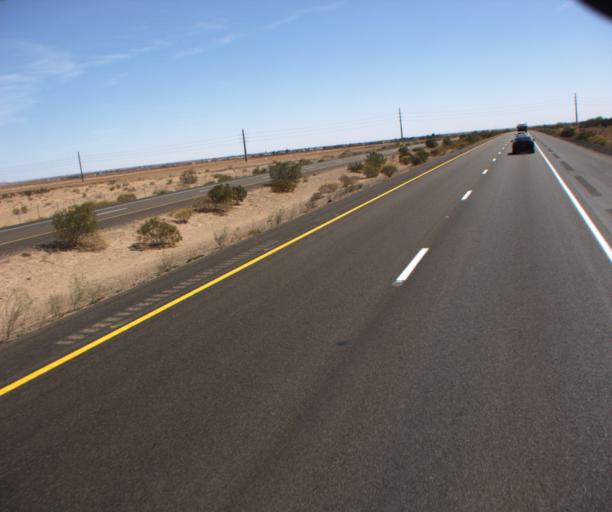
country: US
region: Arizona
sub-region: Yuma County
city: Fortuna Foothills
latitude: 32.6531
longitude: -114.5216
